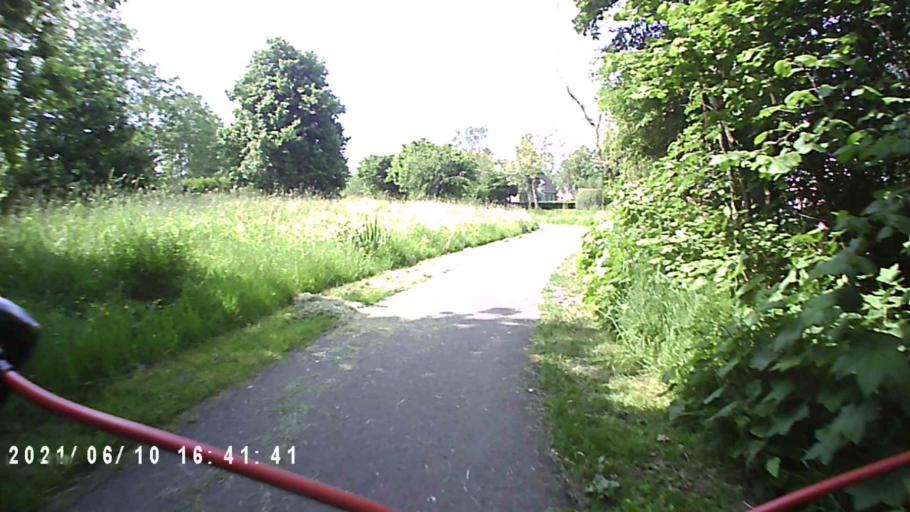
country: NL
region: Friesland
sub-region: Gemeente Achtkarspelen
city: Buitenpost
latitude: 53.2447
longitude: 6.1373
